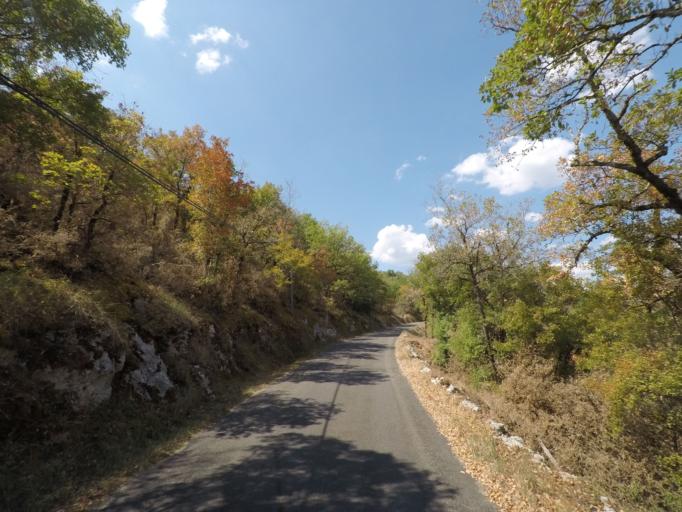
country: FR
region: Midi-Pyrenees
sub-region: Departement du Lot
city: Cajarc
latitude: 44.5148
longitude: 1.6458
